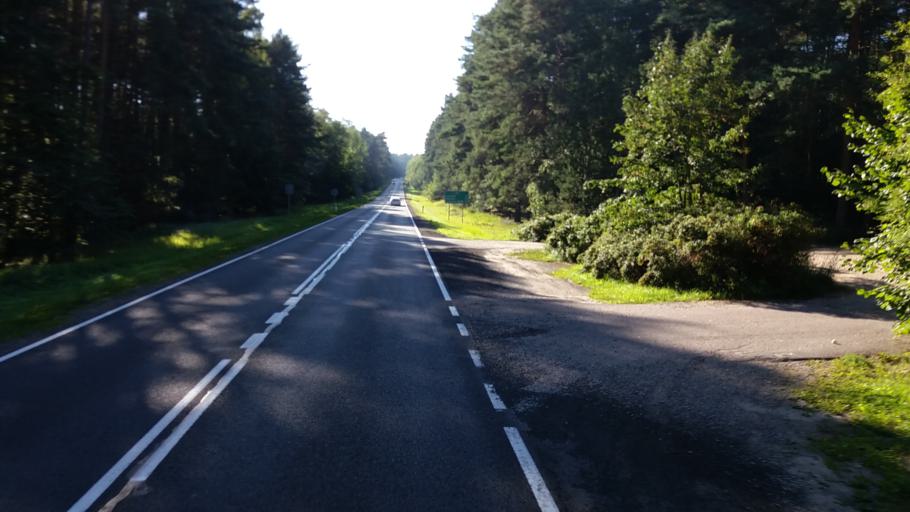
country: PL
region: West Pomeranian Voivodeship
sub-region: Powiat drawski
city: Kalisz Pomorski
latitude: 53.2920
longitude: 15.8793
